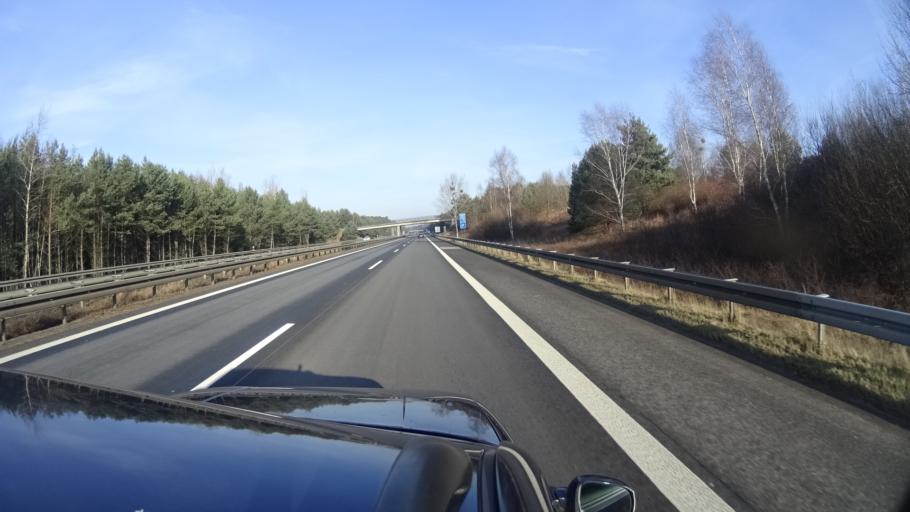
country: DE
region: Berlin
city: Heiligensee
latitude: 52.6439
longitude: 13.2427
